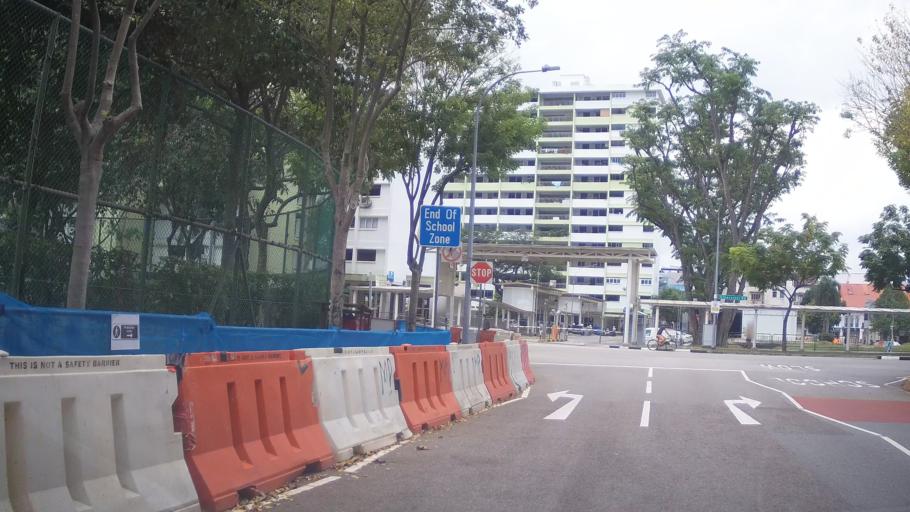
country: SG
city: Singapore
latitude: 1.3126
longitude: 103.8517
